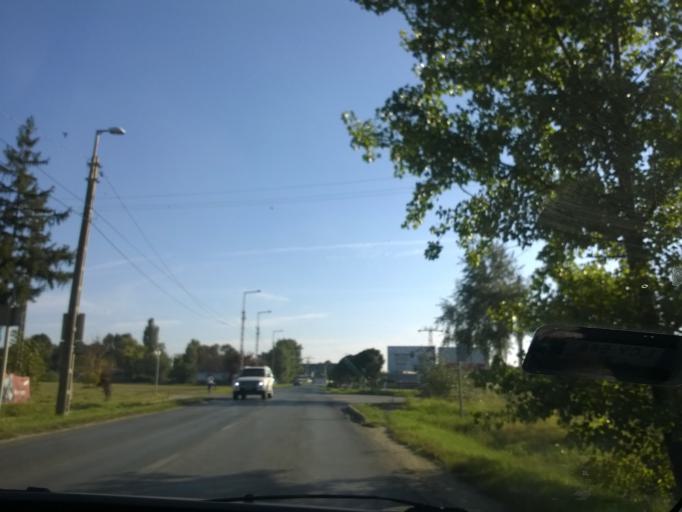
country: HU
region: Pest
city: Szigetszentmiklos
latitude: 47.3583
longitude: 19.0472
